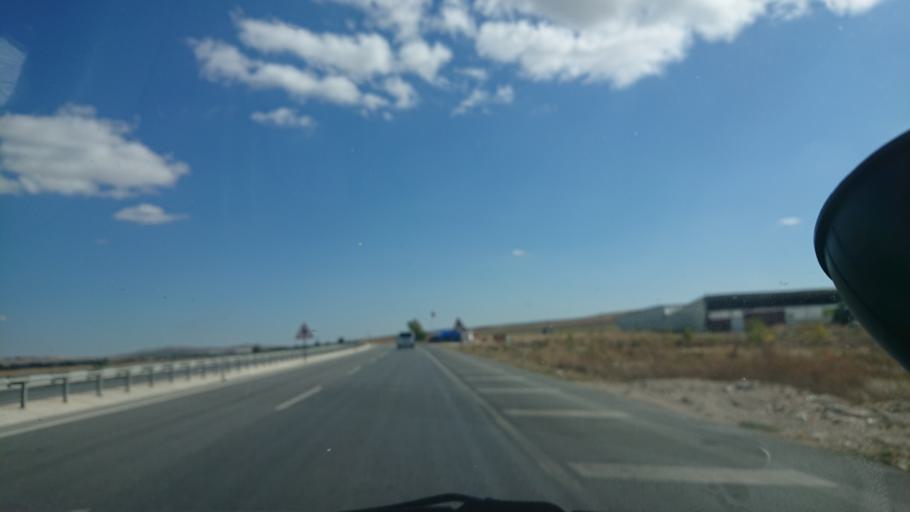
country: TR
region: Eskisehir
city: Mahmudiye
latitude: 39.5336
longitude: 30.9463
